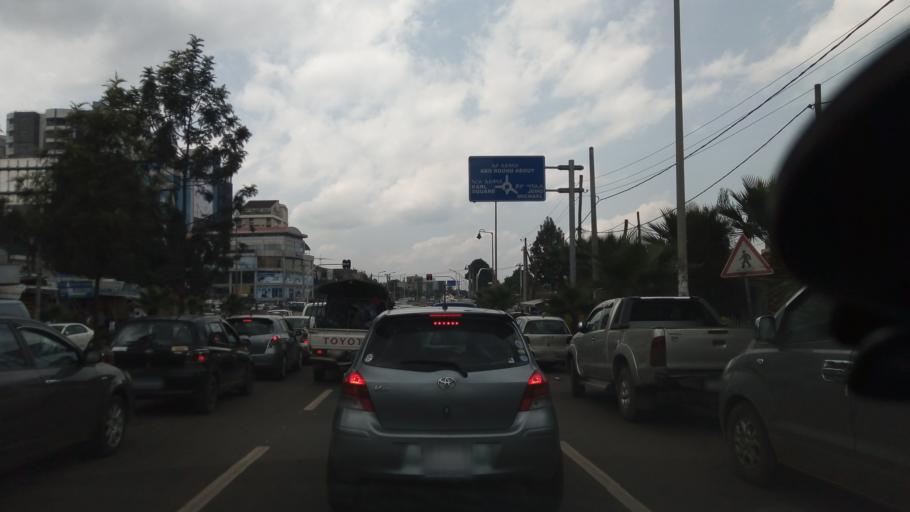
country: ET
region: Adis Abeba
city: Addis Ababa
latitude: 8.9892
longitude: 38.7222
